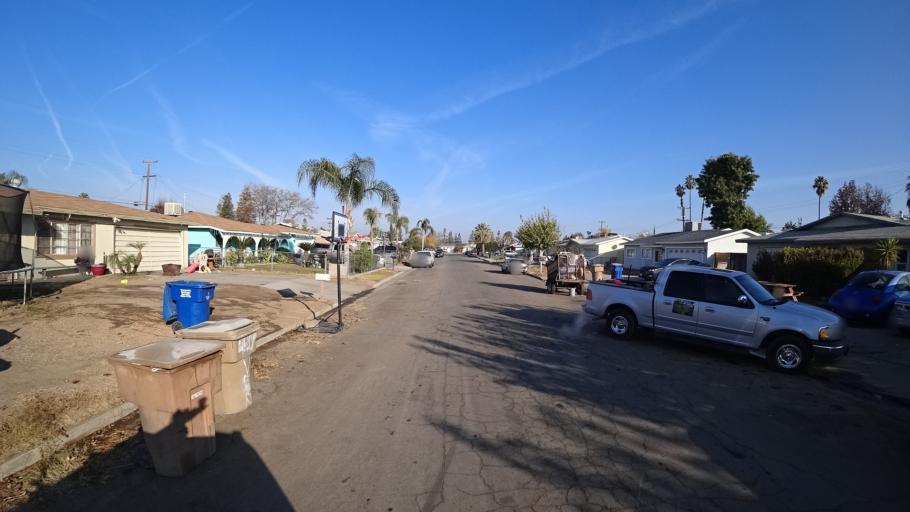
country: US
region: California
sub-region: Kern County
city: Greenfield
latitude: 35.3143
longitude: -119.0065
